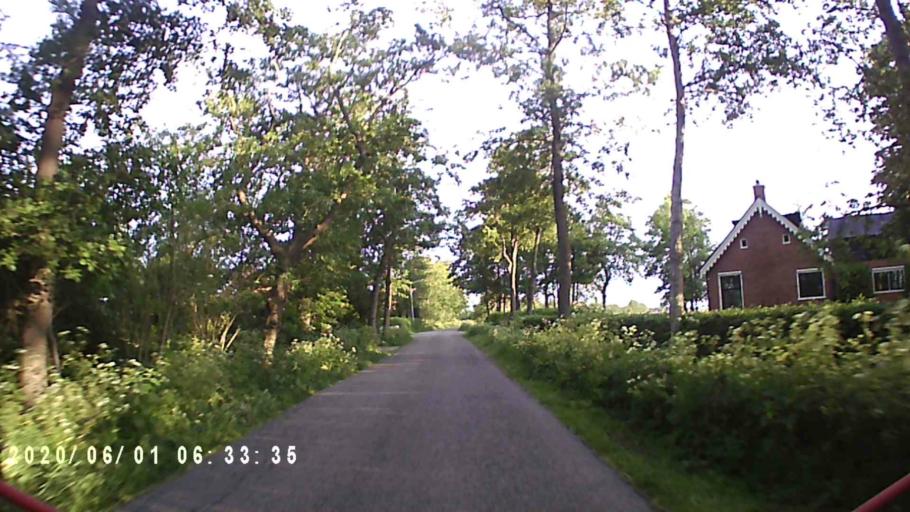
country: NL
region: Friesland
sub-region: Gemeente Kollumerland en Nieuwkruisland
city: Kollum
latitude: 53.2770
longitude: 6.1692
